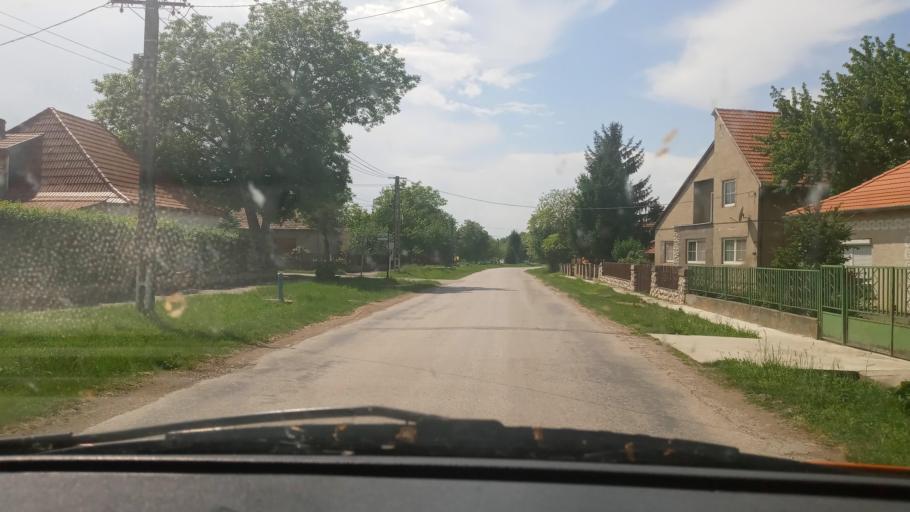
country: HU
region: Baranya
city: Beremend
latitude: 45.8218
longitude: 18.3817
